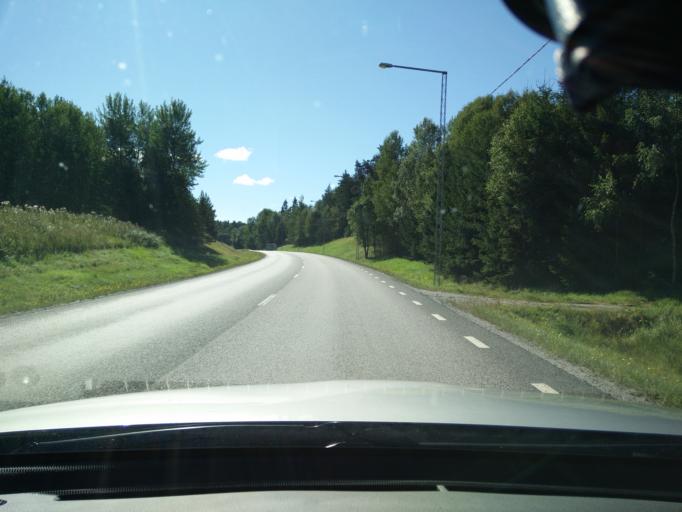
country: SE
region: Stockholm
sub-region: Taby Kommun
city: Taby
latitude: 59.4670
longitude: 18.1160
